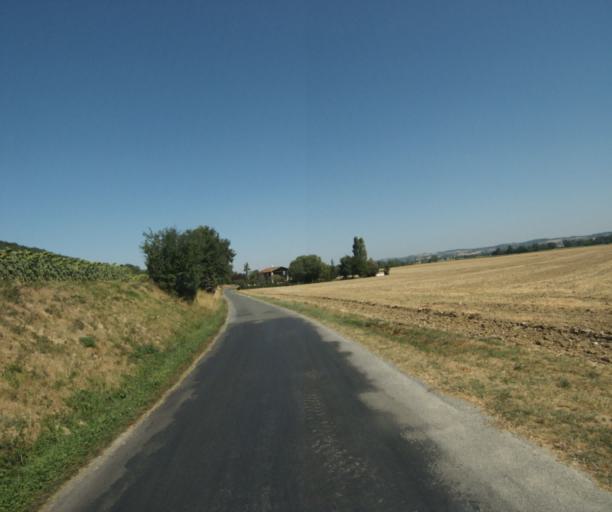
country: FR
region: Midi-Pyrenees
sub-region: Departement de la Haute-Garonne
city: Revel
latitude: 43.5093
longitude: 1.9514
